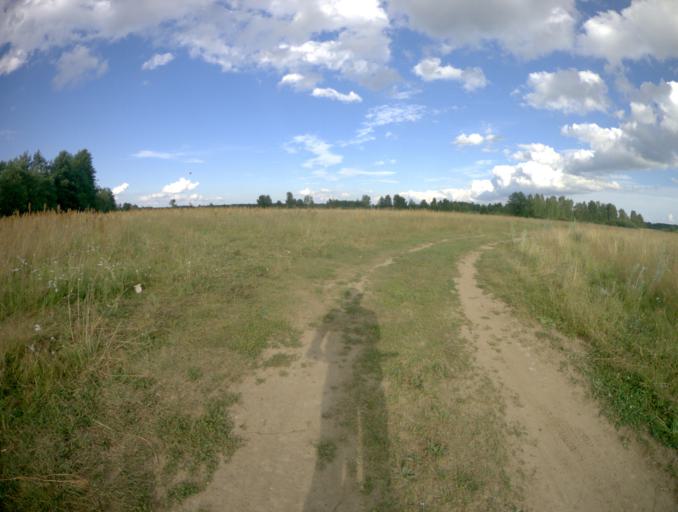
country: RU
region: Vladimir
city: Raduzhnyy
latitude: 56.0395
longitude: 40.3084
